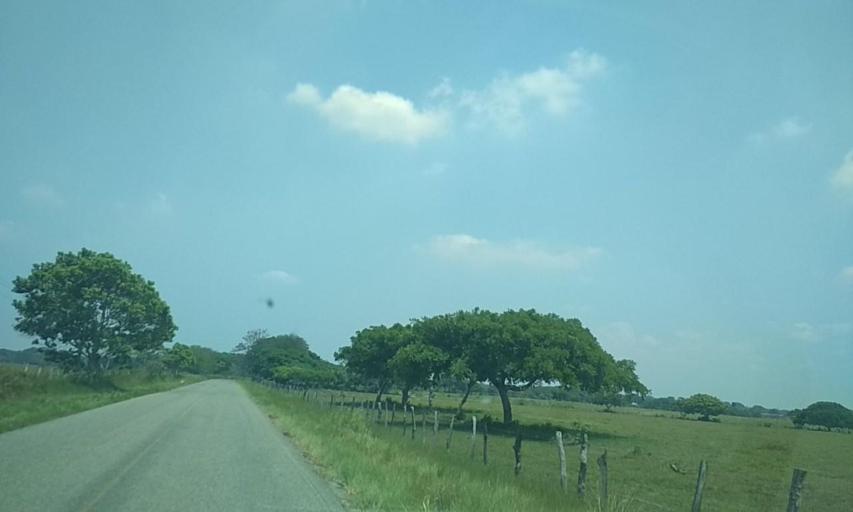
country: MX
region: Tabasco
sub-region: Cardenas
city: Poblado C-33 20 de Noviembre
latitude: 17.8519
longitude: -93.5744
